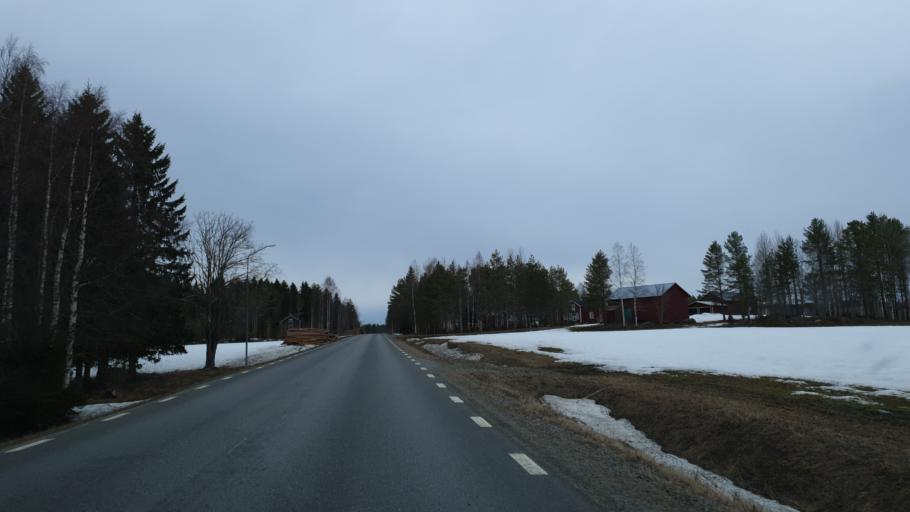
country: SE
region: Vaesterbotten
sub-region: Robertsfors Kommun
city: Robertsfors
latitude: 64.3844
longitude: 20.8976
